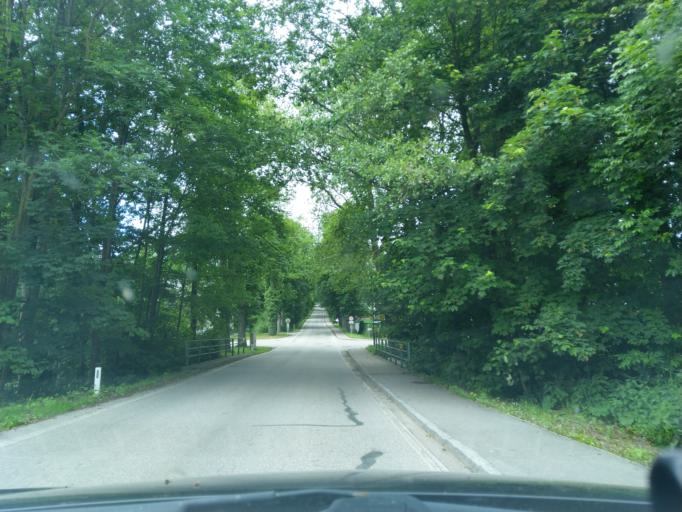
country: AT
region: Upper Austria
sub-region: Politischer Bezirk Ried im Innkreis
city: Ried im Innkreis
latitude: 48.2906
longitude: 13.4329
